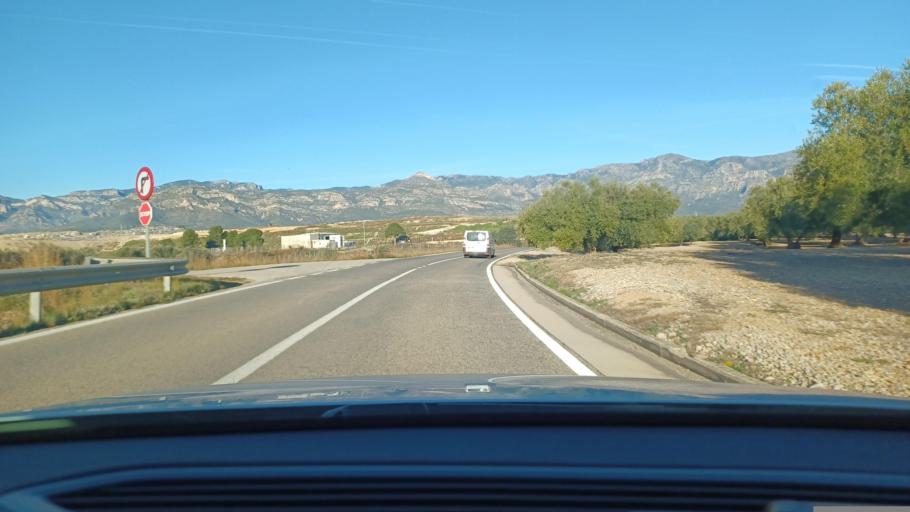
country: ES
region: Catalonia
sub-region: Provincia de Tarragona
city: Mas de Barberans
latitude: 40.7125
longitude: 0.4052
